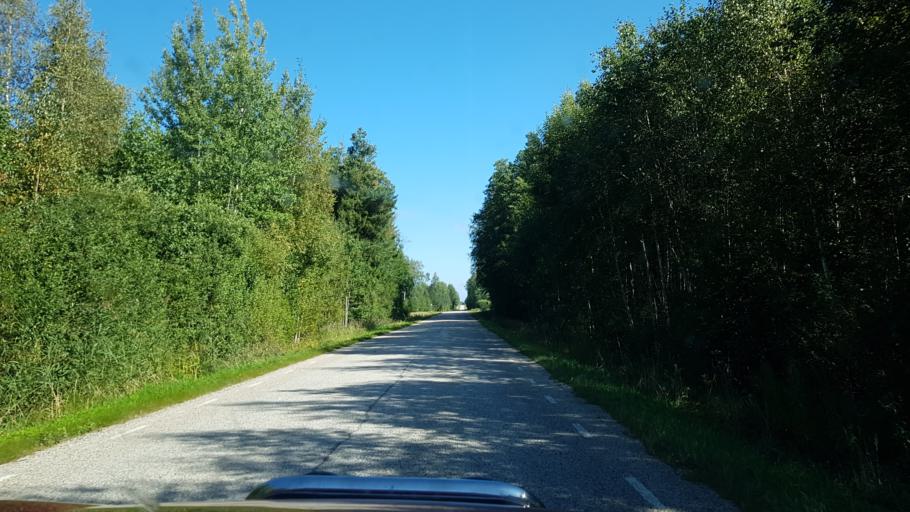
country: EE
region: Polvamaa
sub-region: Raepina vald
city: Rapina
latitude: 58.2228
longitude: 27.2875
